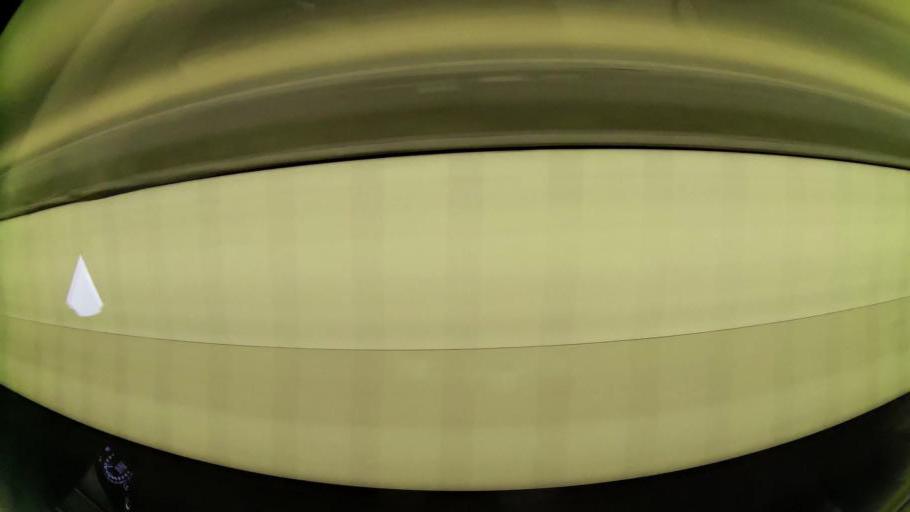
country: HK
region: Sha Tin
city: Sha Tin
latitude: 22.3793
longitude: 114.1607
